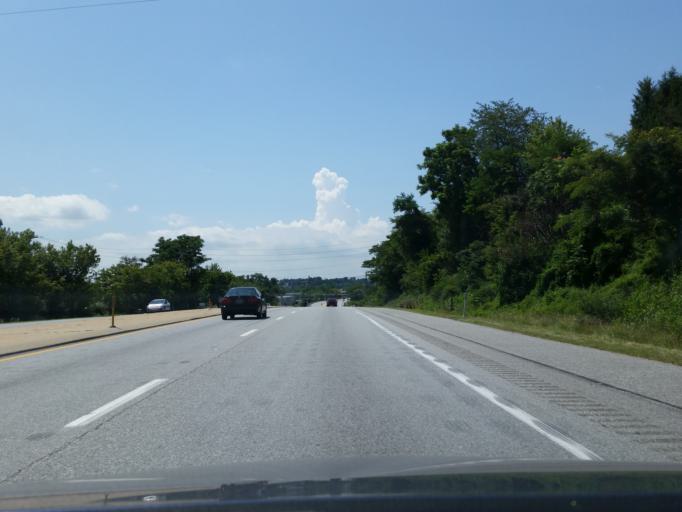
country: US
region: Pennsylvania
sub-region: York County
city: East York
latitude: 39.9825
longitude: -76.7037
